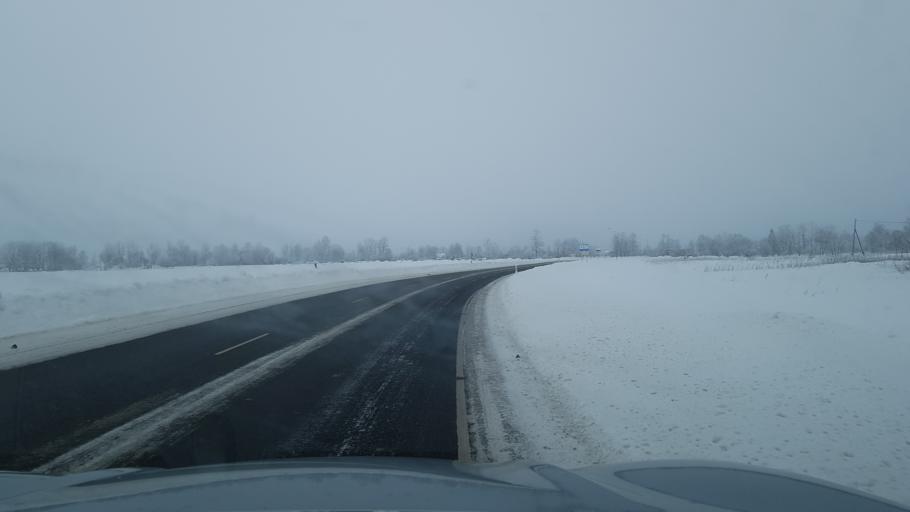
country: EE
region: Ida-Virumaa
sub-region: Johvi vald
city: Johvi
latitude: 59.3265
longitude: 27.3998
